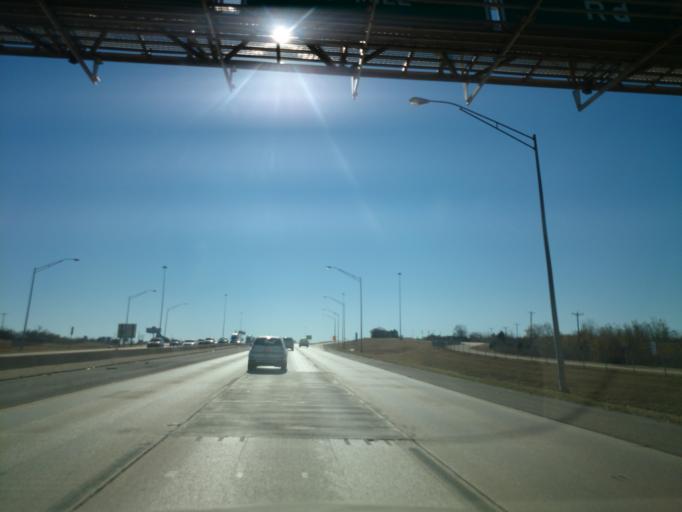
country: US
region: Oklahoma
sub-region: Oklahoma County
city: Edmond
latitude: 35.6162
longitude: -97.4251
